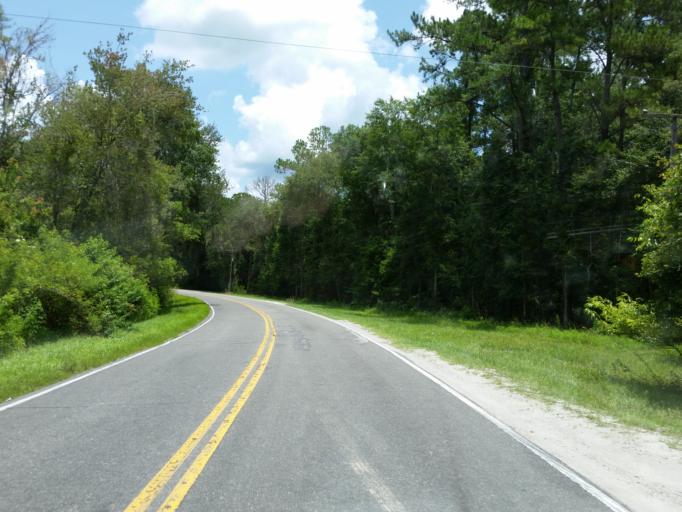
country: US
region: Florida
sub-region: Alachua County
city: Gainesville
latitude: 29.4980
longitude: -82.2920
